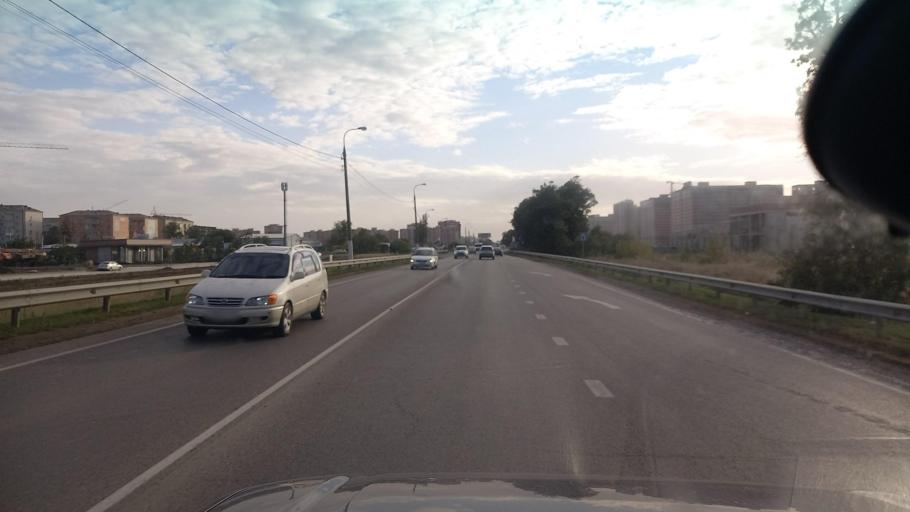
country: RU
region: Krasnodarskiy
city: Krasnodar
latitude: 45.1018
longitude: 38.9157
